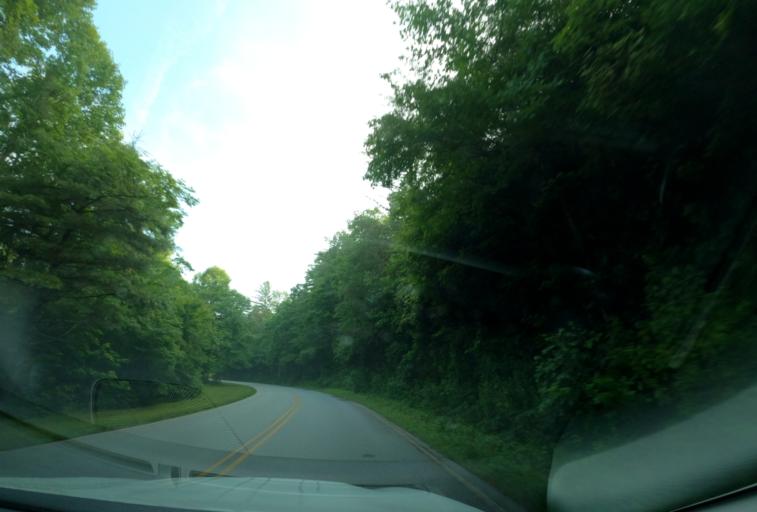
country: US
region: North Carolina
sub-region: Transylvania County
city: Brevard
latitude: 35.2355
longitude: -82.8726
